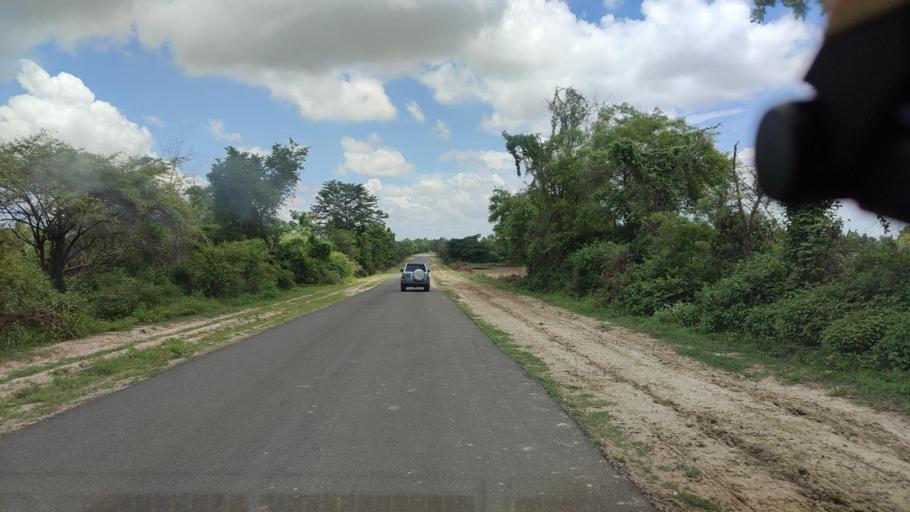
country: MM
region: Magway
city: Taungdwingyi
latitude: 20.1531
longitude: 95.5769
